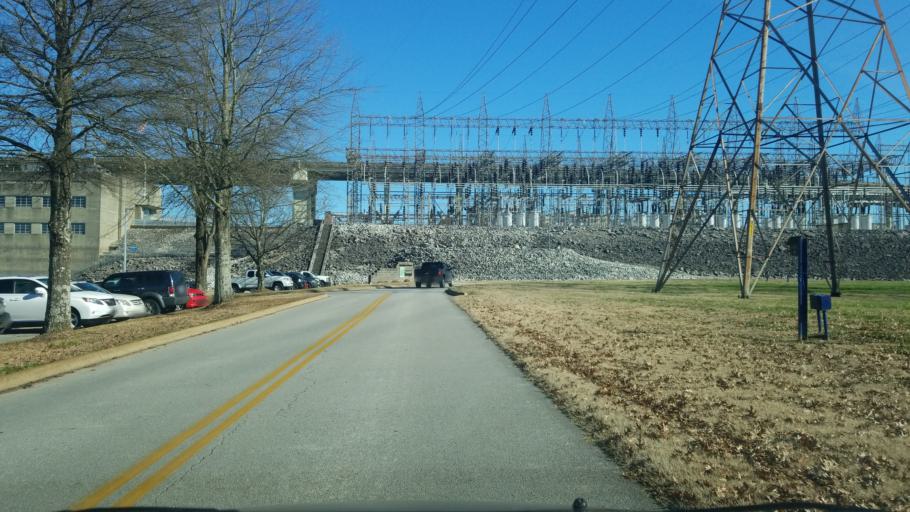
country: US
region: Tennessee
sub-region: Hamilton County
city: East Chattanooga
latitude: 35.1019
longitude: -85.2310
